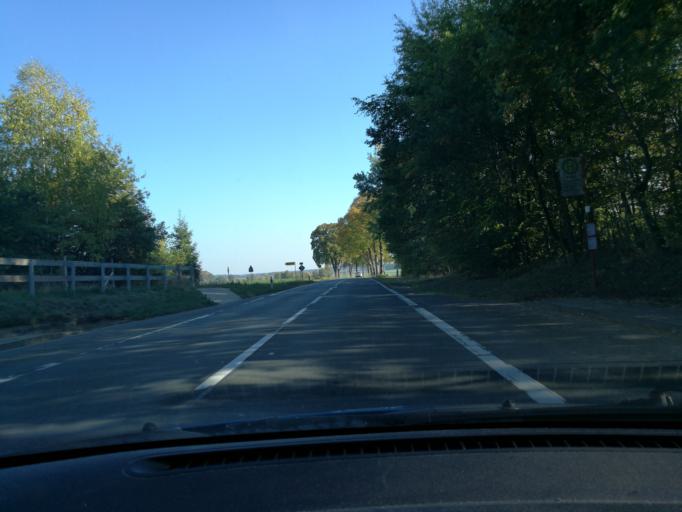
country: DE
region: Lower Saxony
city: Nahrendorf
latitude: 53.1711
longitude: 10.7798
